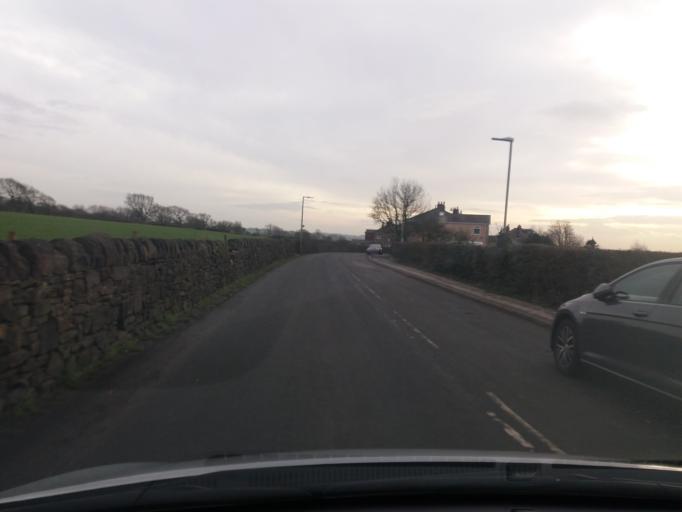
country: GB
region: England
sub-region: Lancashire
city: Adlington
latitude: 53.6248
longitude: -2.5894
